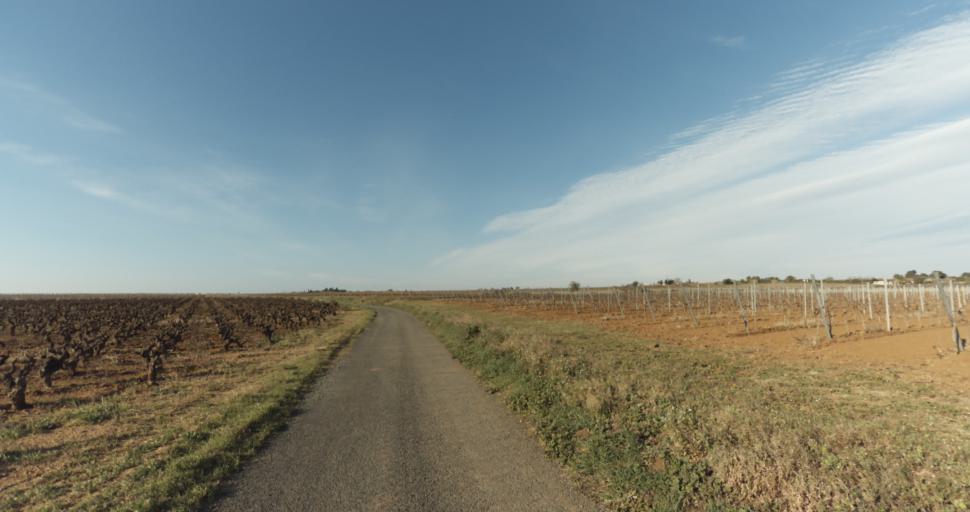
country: FR
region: Languedoc-Roussillon
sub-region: Departement de l'Herault
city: Marseillan
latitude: 43.3703
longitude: 3.5176
